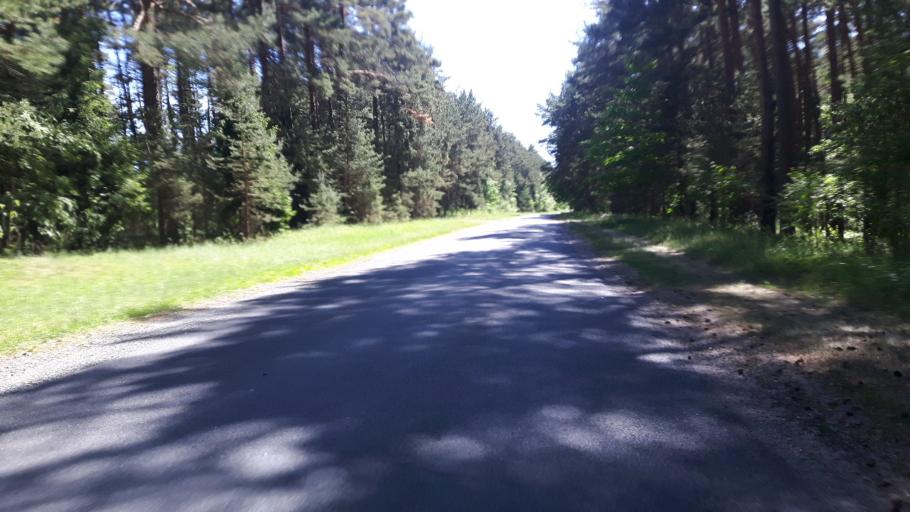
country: LV
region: Salacgrivas
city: Ainazi
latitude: 57.8987
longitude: 24.3745
